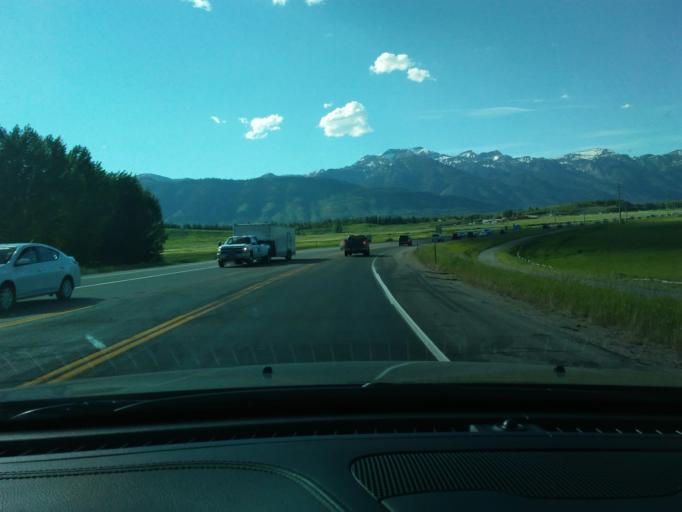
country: US
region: Wyoming
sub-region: Teton County
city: Moose Wilson Road
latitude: 43.4841
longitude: -110.8262
